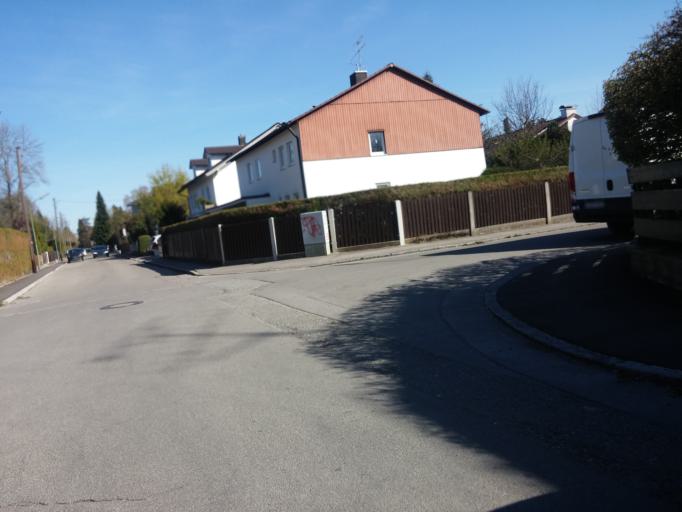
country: DE
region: Bavaria
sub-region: Upper Bavaria
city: Neubiberg
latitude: 48.0818
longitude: 11.6690
